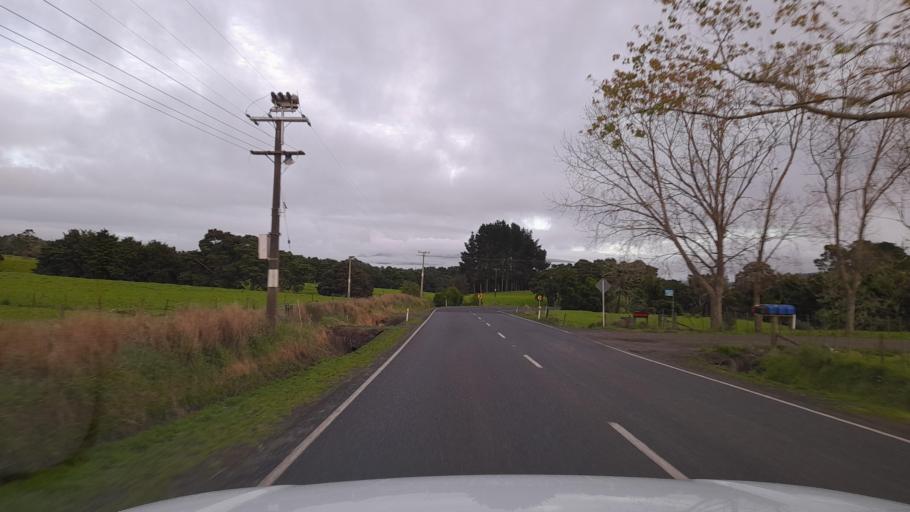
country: NZ
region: Northland
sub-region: Whangarei
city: Maungatapere
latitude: -35.7271
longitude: 174.0443
